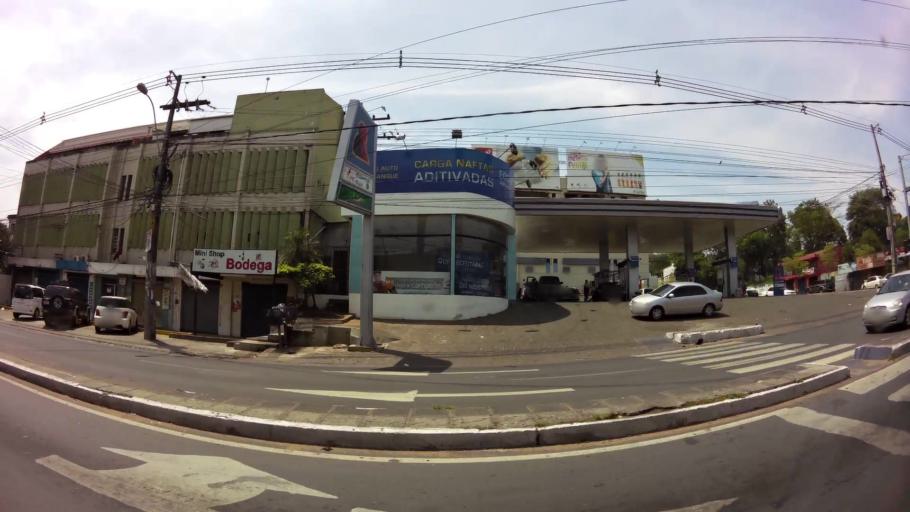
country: PY
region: Central
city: Lambare
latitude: -25.3083
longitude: -57.5963
